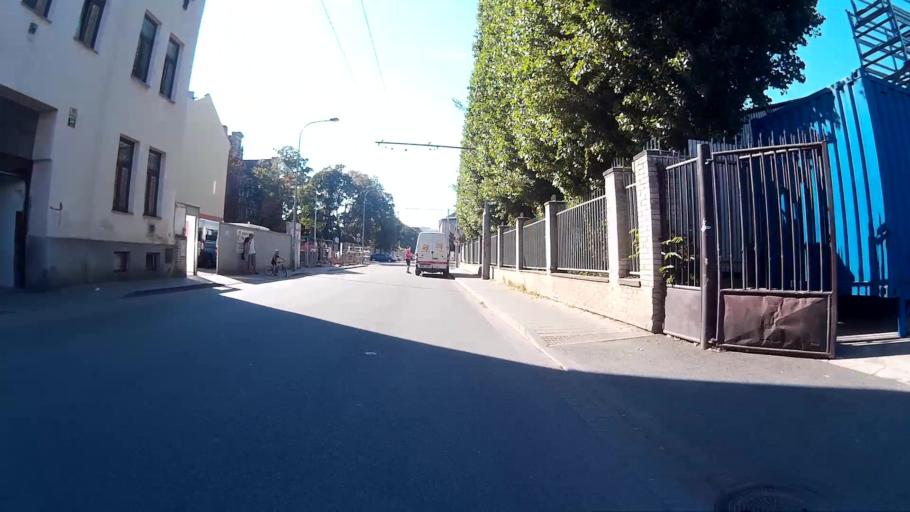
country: CZ
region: South Moravian
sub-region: Mesto Brno
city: Brno
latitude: 49.1896
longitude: 16.6217
